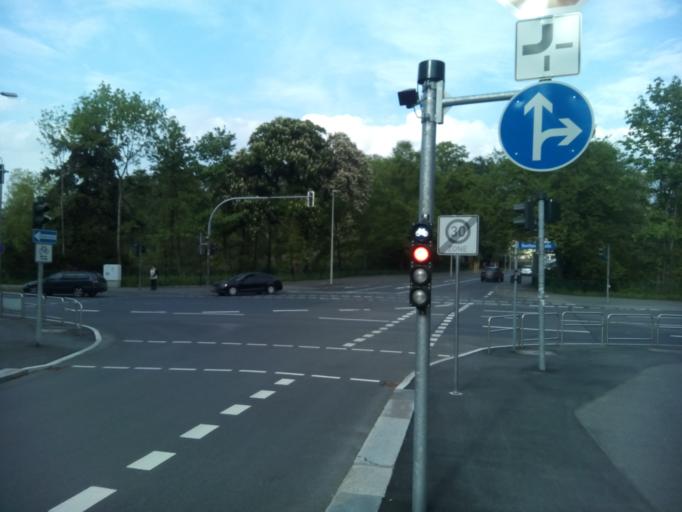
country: DE
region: Saxony
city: Freiberg
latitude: 50.9196
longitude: 13.3375
